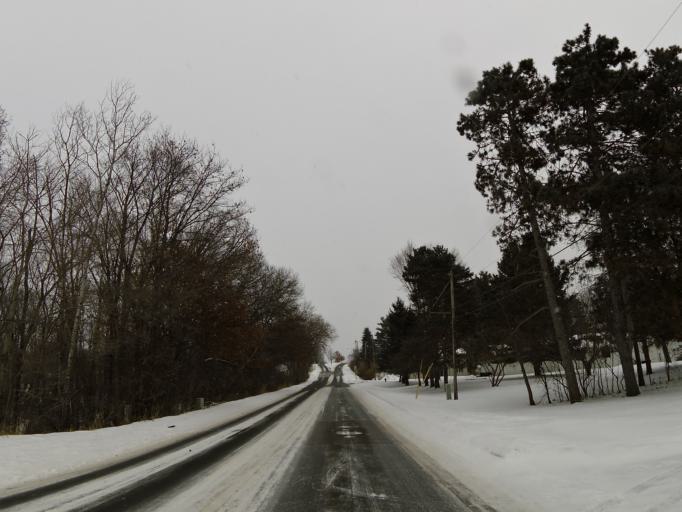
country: US
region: Minnesota
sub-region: Washington County
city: Lake Elmo
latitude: 44.9924
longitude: -92.8741
